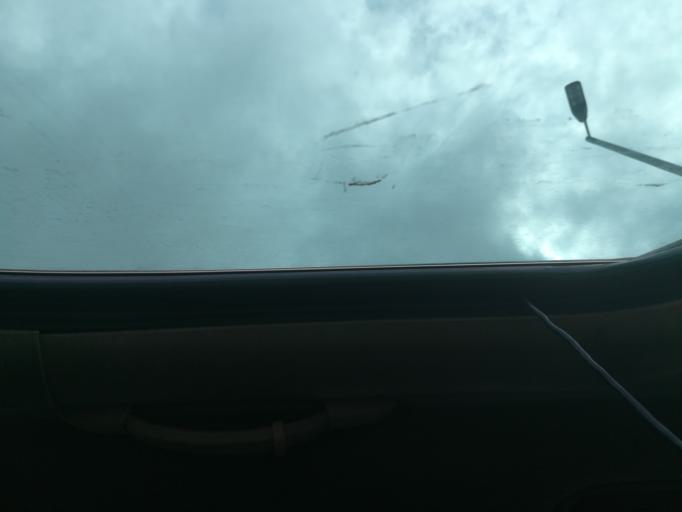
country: NG
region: Lagos
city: Lagos
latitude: 6.4135
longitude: 3.4114
